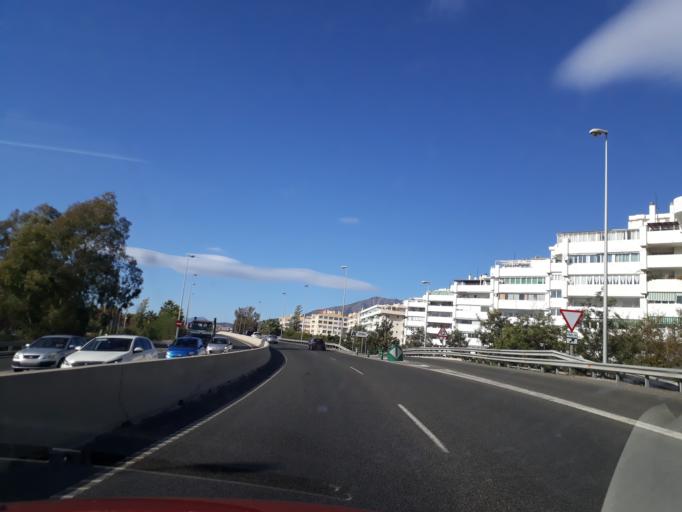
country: ES
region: Andalusia
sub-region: Provincia de Malaga
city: Fuengirola
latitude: 36.5300
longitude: -4.6289
